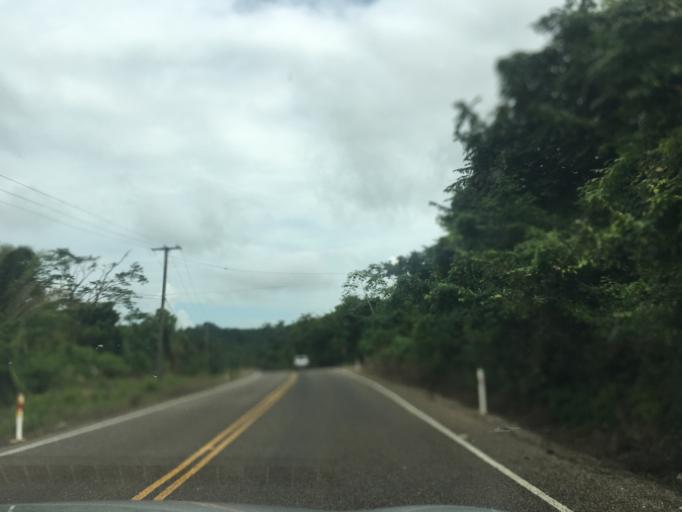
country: BZ
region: Cayo
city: Belmopan
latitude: 17.2012
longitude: -88.7745
